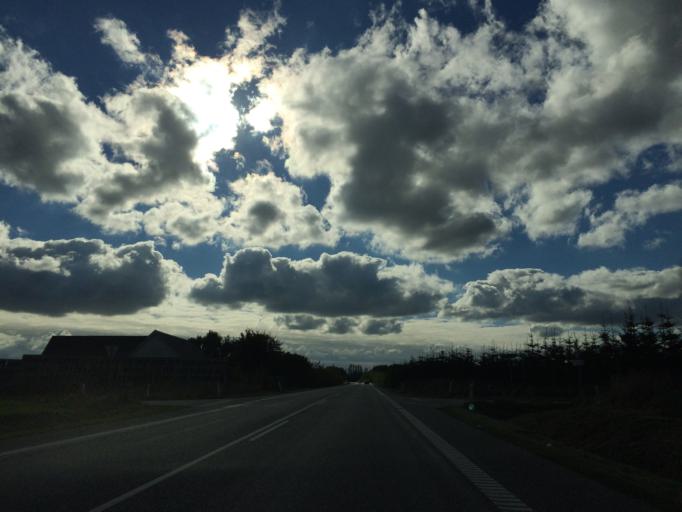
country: DK
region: Central Jutland
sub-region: Skanderborg Kommune
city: Ry
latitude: 56.1411
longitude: 9.8021
